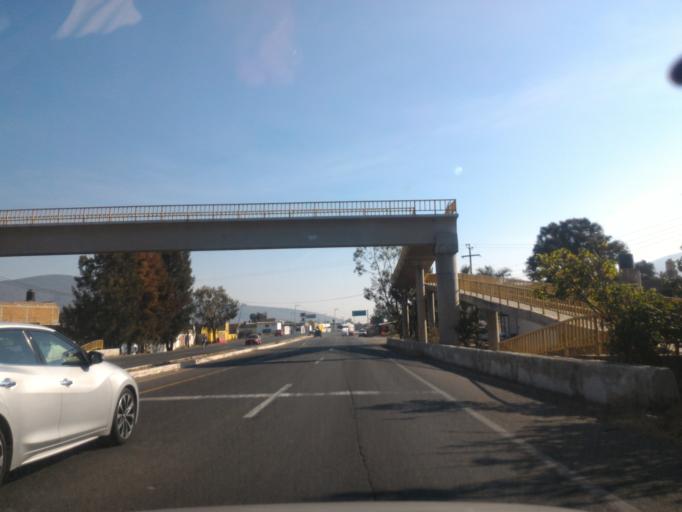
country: MX
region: Jalisco
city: Atequiza
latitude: 20.3916
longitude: -103.1335
